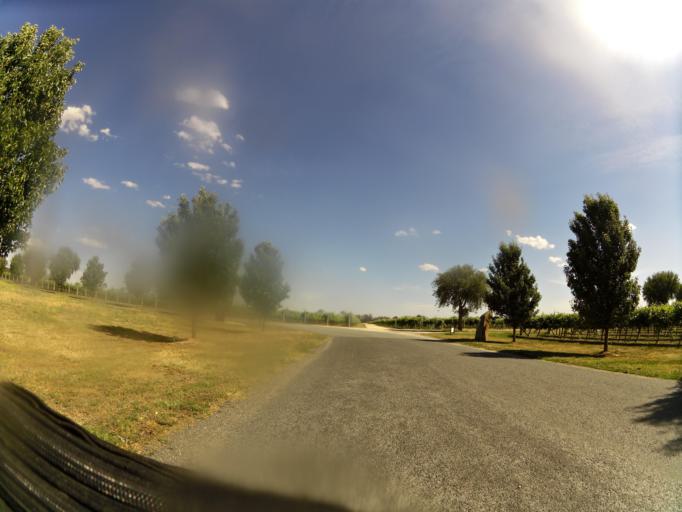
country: AU
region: Victoria
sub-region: Campaspe
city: Kyabram
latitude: -36.8531
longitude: 145.0899
